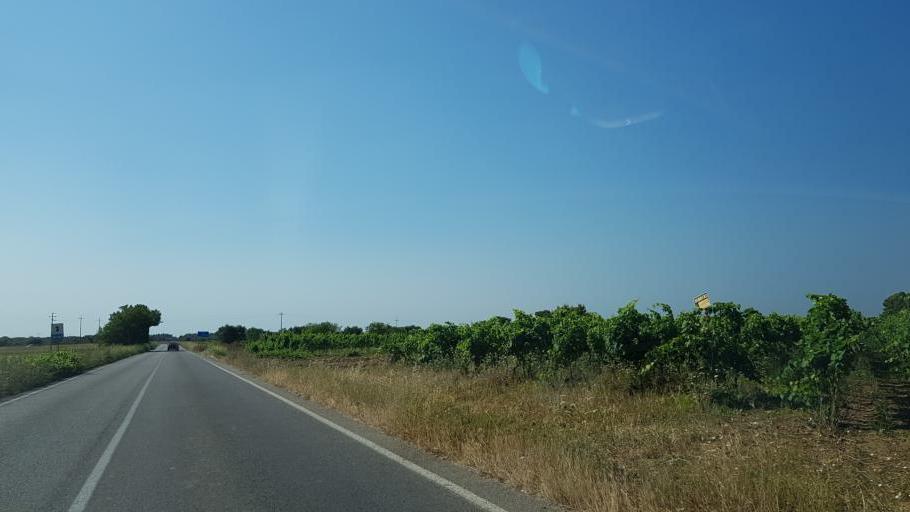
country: IT
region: Apulia
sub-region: Provincia di Lecce
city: Guagnano
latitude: 40.4245
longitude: 17.9470
